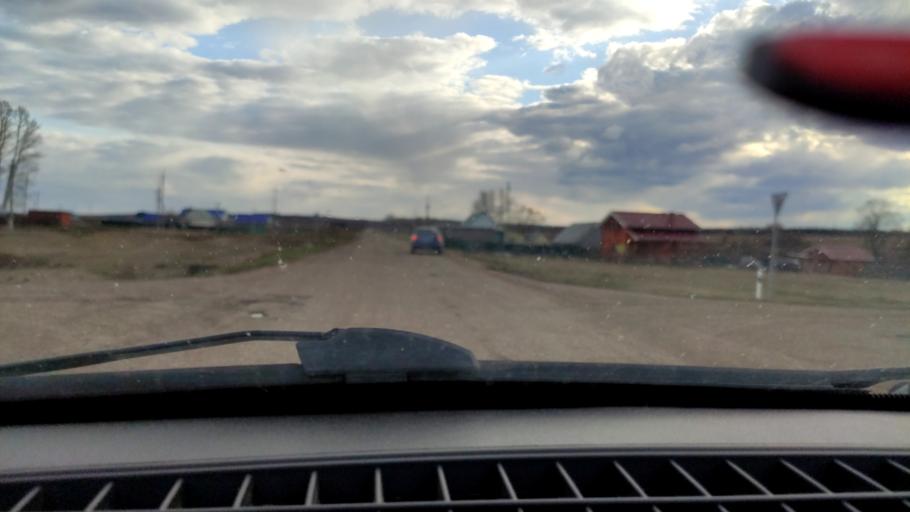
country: RU
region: Bashkortostan
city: Karmaskaly
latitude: 54.3326
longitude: 55.9941
